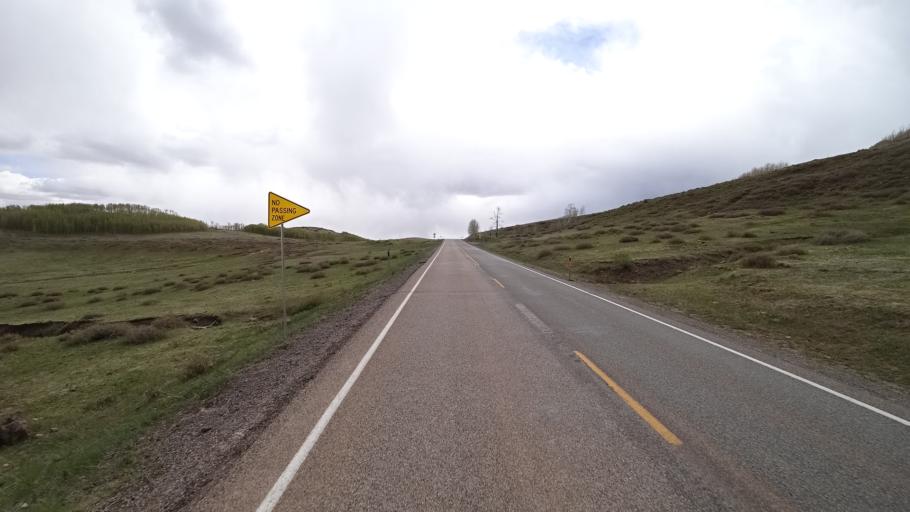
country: US
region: Utah
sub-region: Wayne County
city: Loa
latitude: 38.0386
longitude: -111.3295
